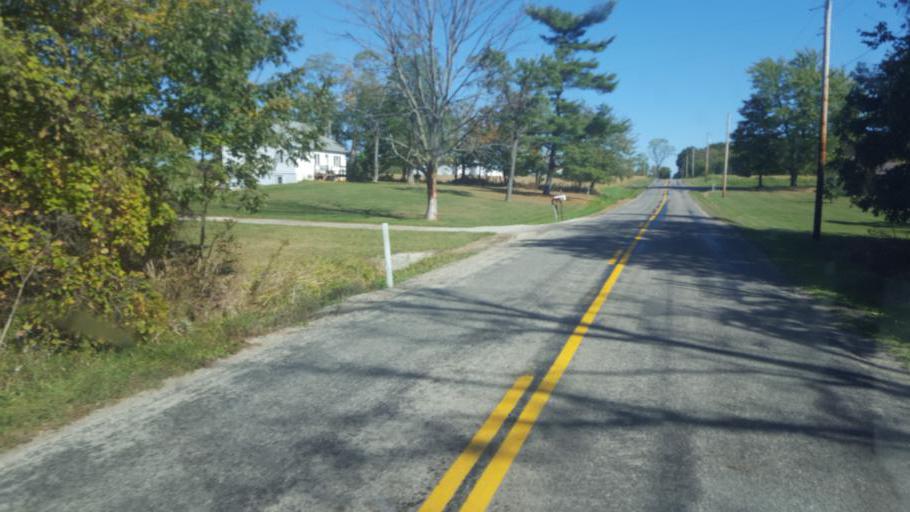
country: US
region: Ohio
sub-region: Huron County
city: New London
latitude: 40.9929
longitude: -82.3520
